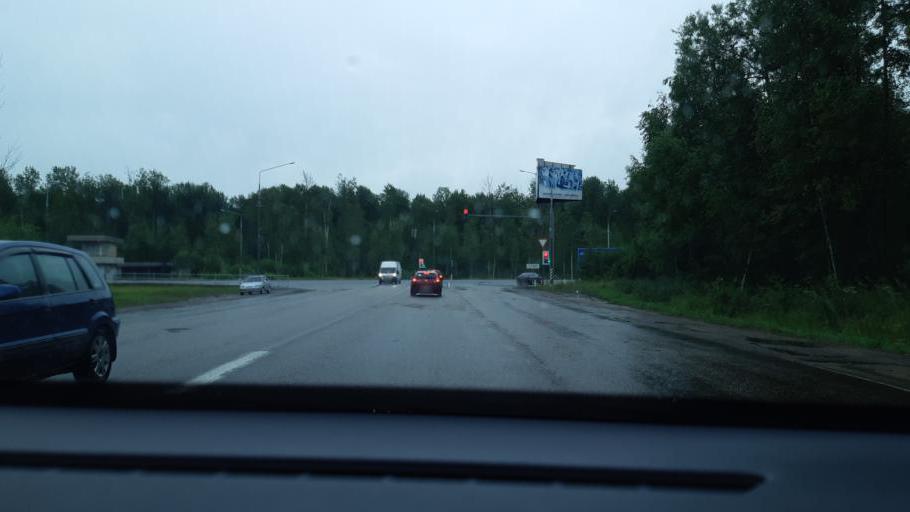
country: RU
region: Smolensk
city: Gagarin
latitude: 55.5005
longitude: 35.0363
